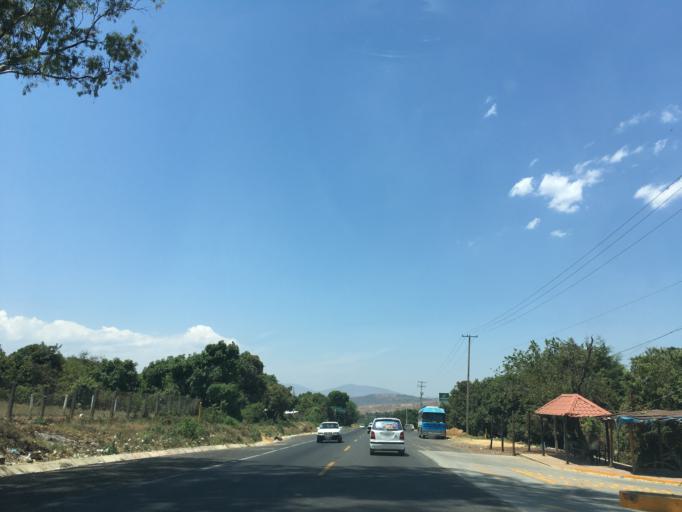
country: MX
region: Michoacan
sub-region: Chilchota
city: Tacuro (Santa Maria Tacuro)
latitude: 19.8530
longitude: -102.0388
